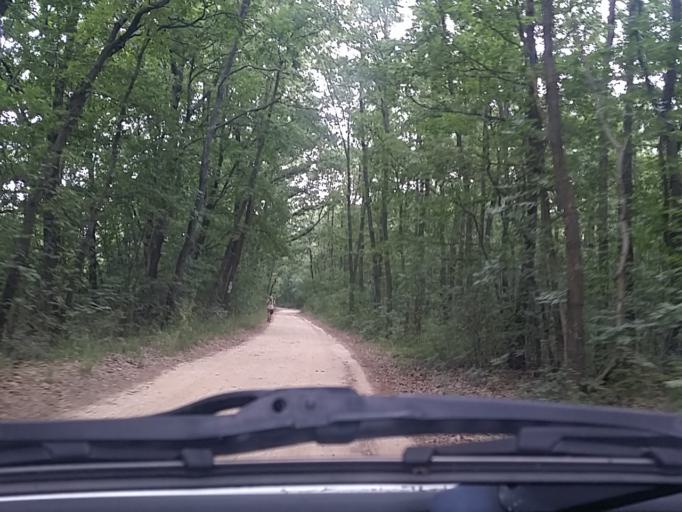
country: HU
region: Pest
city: Csobanka
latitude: 47.6483
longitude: 18.9435
